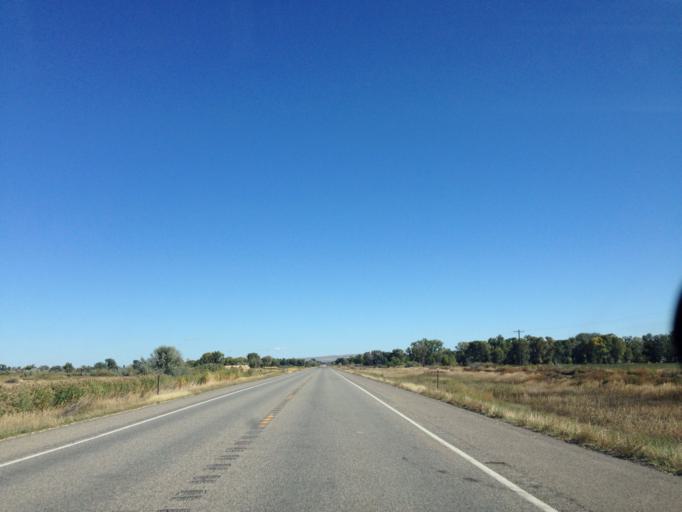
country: US
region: Montana
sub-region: Yellowstone County
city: Laurel
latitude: 45.4036
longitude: -108.8996
